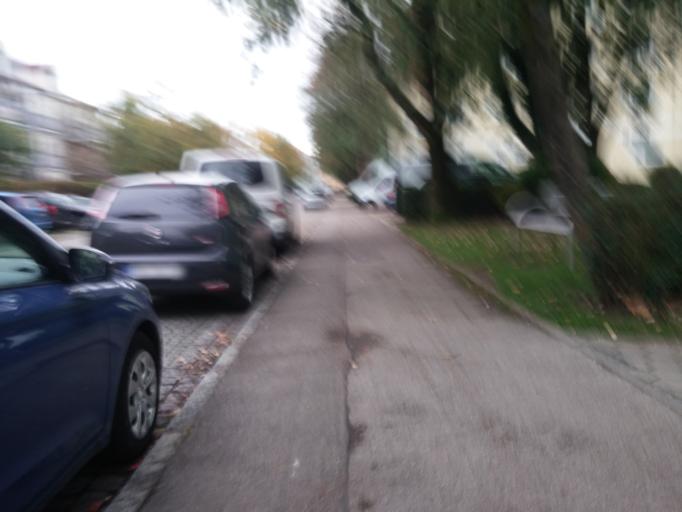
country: DE
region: Bavaria
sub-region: Upper Bavaria
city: Kirchseeon
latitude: 48.0738
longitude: 11.8848
